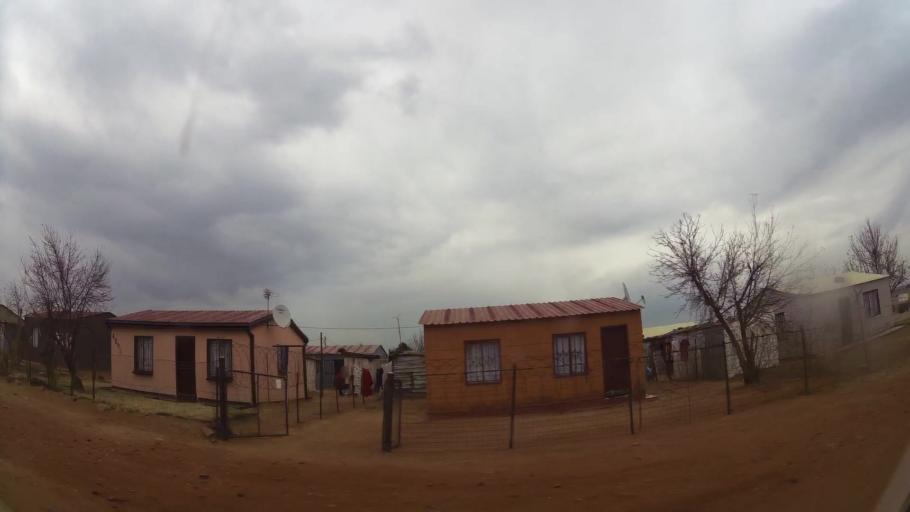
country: ZA
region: Gauteng
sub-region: Ekurhuleni Metropolitan Municipality
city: Germiston
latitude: -26.3828
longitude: 28.1401
